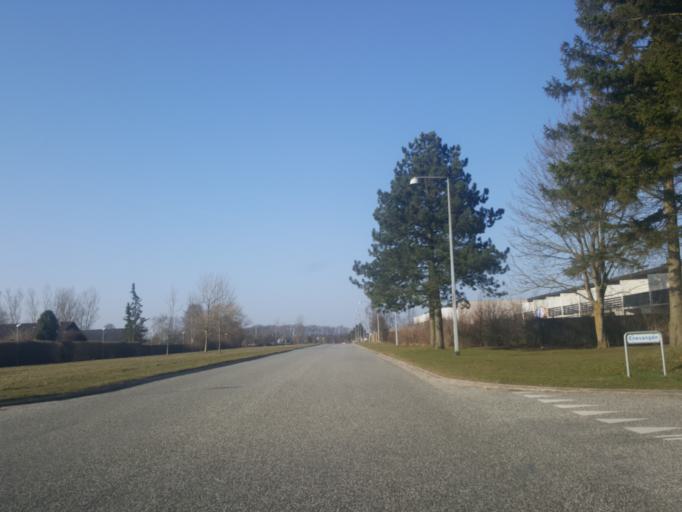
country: DK
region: Capital Region
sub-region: Allerod Kommune
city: Lillerod
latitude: 55.8706
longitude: 12.3288
